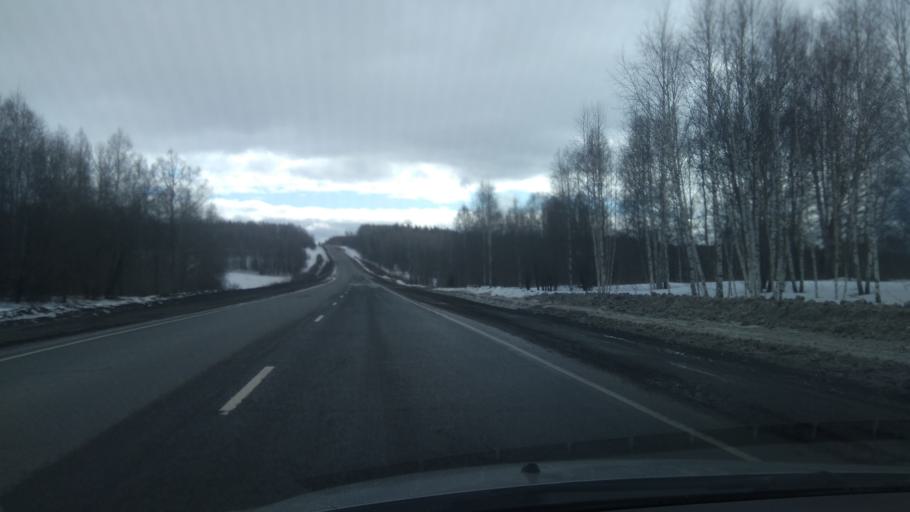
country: RU
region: Perm
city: Ust'-Kishert'
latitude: 57.1815
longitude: 57.1295
